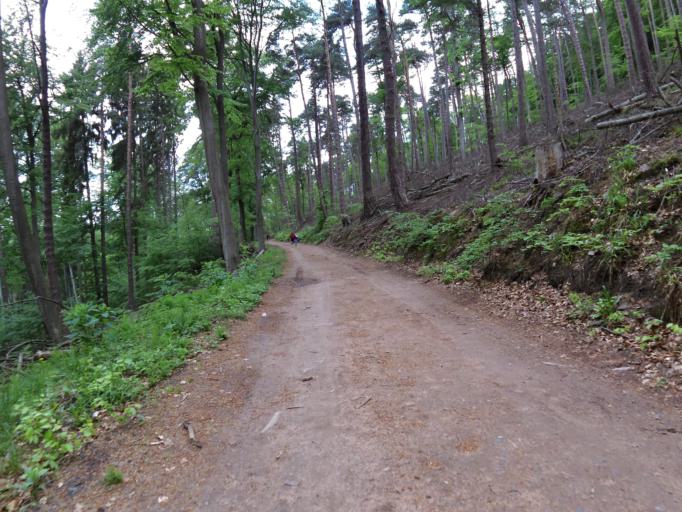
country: DE
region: Rheinland-Pfalz
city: Neidenfels
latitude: 49.4070
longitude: 8.0640
